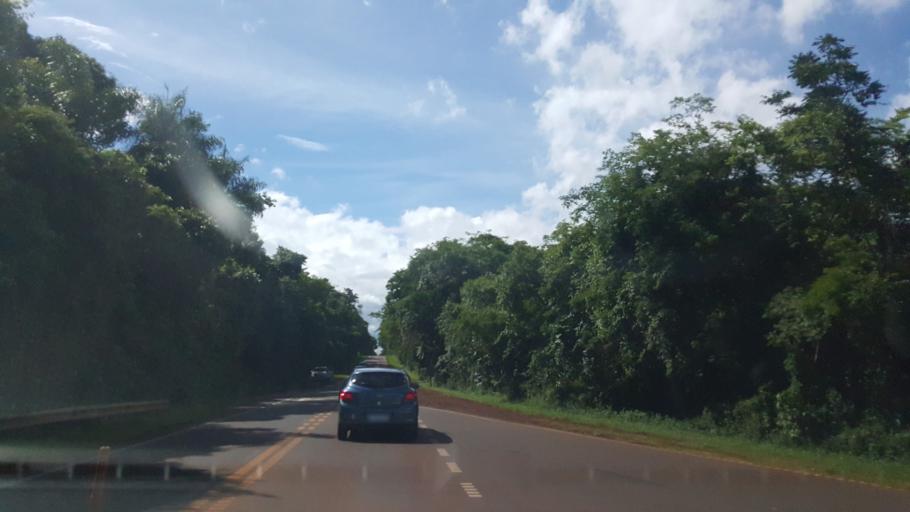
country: AR
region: Misiones
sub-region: Departamento de Iguazu
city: Puerto Iguazu
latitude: -25.6907
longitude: -54.4781
